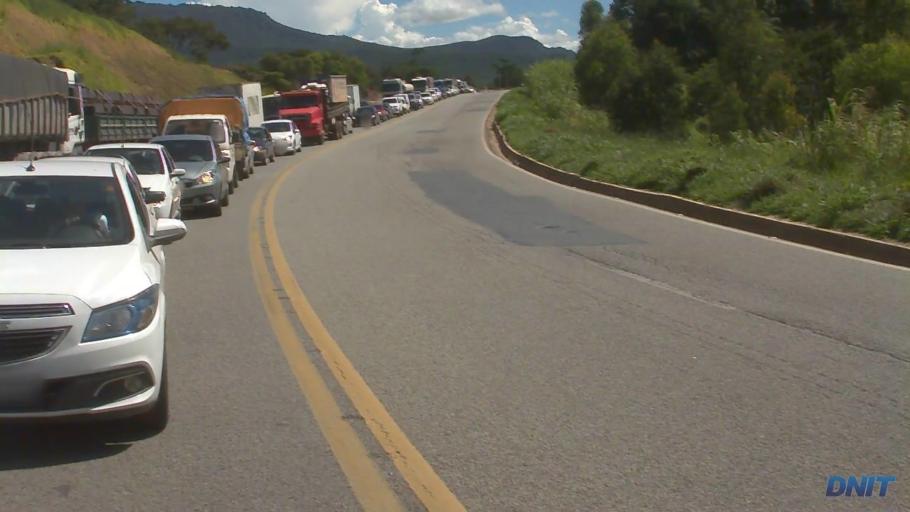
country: BR
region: Minas Gerais
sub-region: Caete
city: Caete
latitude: -19.7830
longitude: -43.6611
